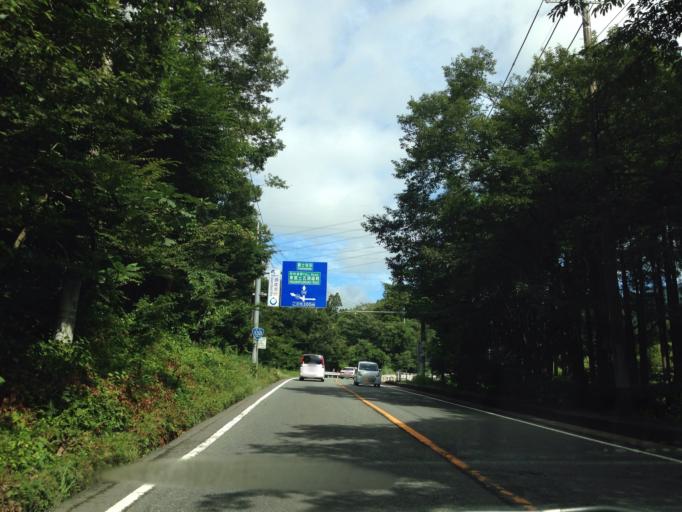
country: JP
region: Shizuoka
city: Gotemba
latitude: 35.3509
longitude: 138.8757
